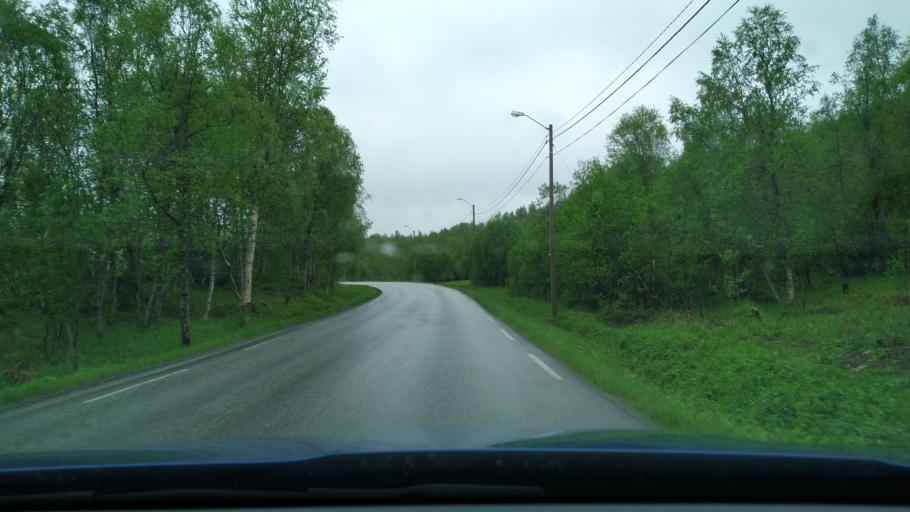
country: NO
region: Troms
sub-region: Dyroy
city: Brostadbotn
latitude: 69.0519
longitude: 17.7307
